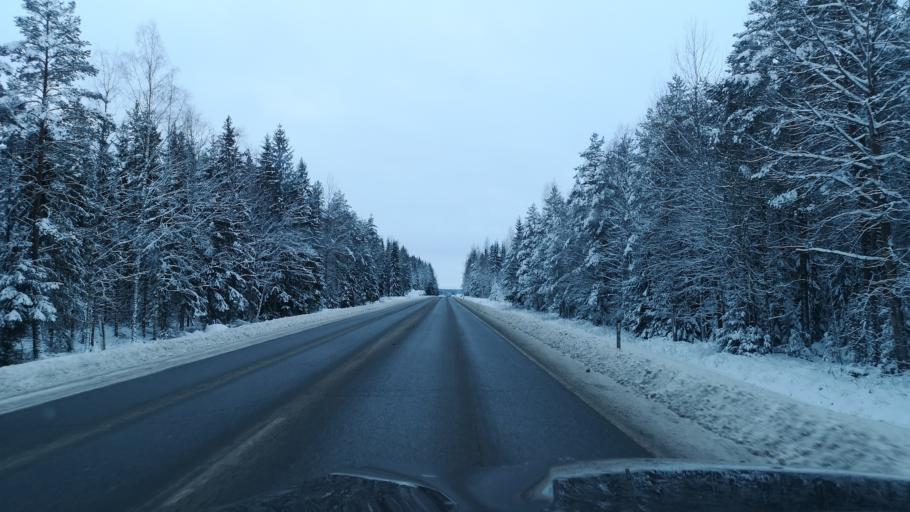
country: FI
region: Varsinais-Suomi
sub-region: Loimaa
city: Loimaa
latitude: 60.9014
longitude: 23.1400
